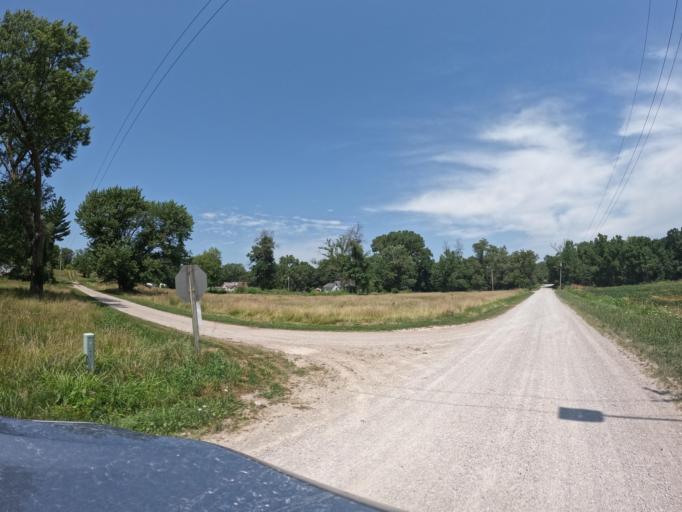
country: US
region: Iowa
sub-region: Appanoose County
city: Centerville
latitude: 40.7744
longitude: -92.9493
